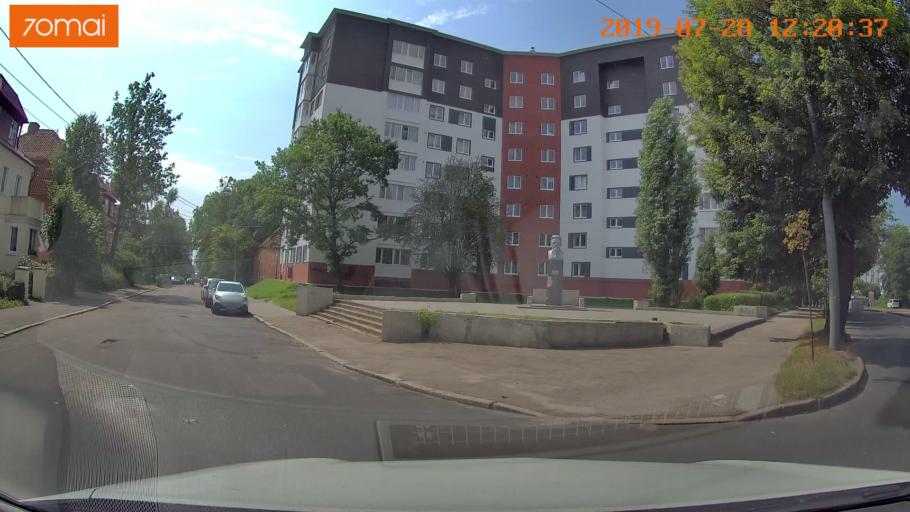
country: RU
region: Kaliningrad
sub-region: Gorod Kaliningrad
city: Kaliningrad
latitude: 54.7136
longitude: 20.4536
